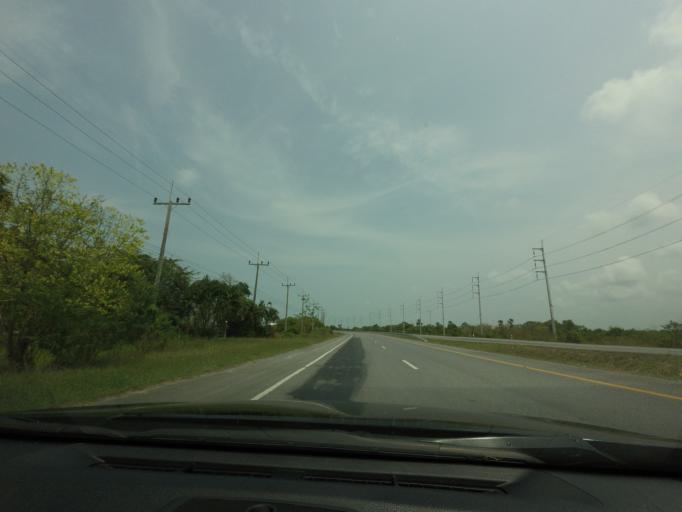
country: TH
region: Nakhon Si Thammarat
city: Hua Sai
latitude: 8.0010
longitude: 100.3053
